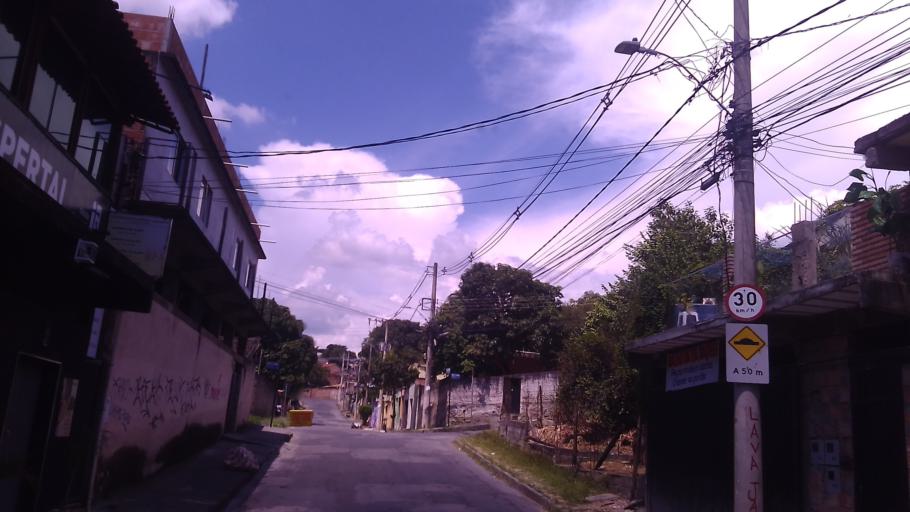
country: BR
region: Minas Gerais
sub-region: Belo Horizonte
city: Belo Horizonte
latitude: -19.8602
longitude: -43.9039
